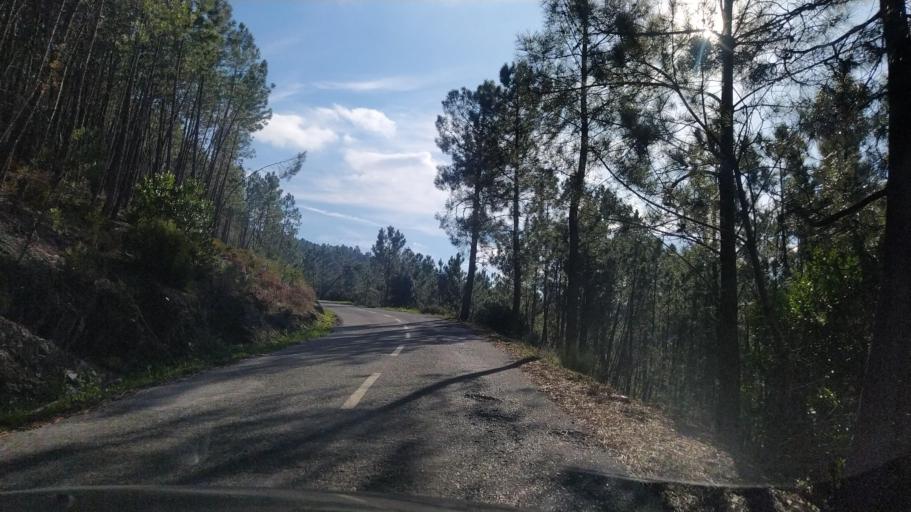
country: PT
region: Coimbra
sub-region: Oliveira do Hospital
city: Oliveira do Hospital
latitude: 40.2049
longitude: -7.7307
